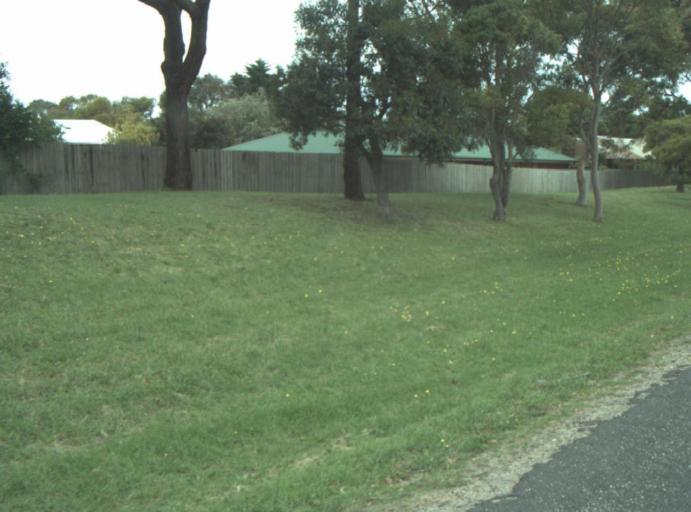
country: AU
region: Victoria
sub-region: Queenscliffe
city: Queenscliff
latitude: -38.2715
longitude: 144.6120
